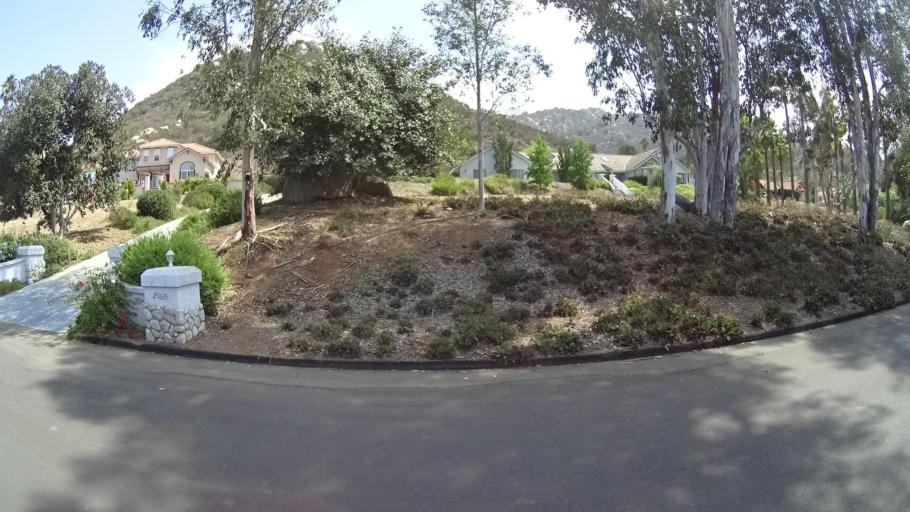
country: US
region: California
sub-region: San Diego County
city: Hidden Meadows
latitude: 33.1804
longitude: -117.0790
